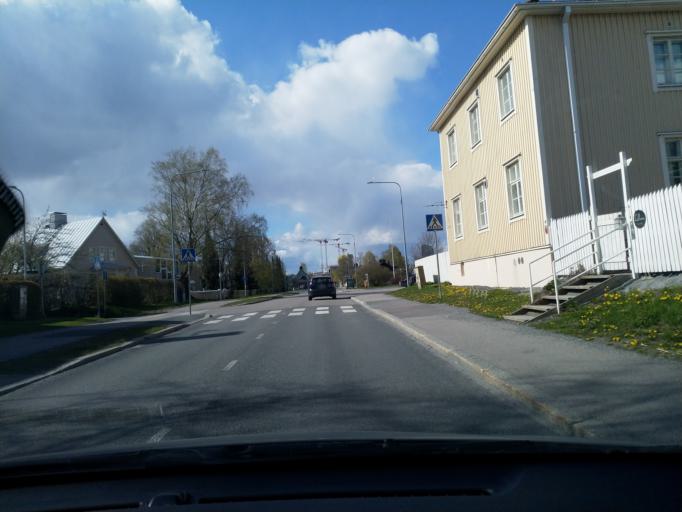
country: FI
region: Pirkanmaa
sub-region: Tampere
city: Tampere
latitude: 61.4857
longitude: 23.7856
